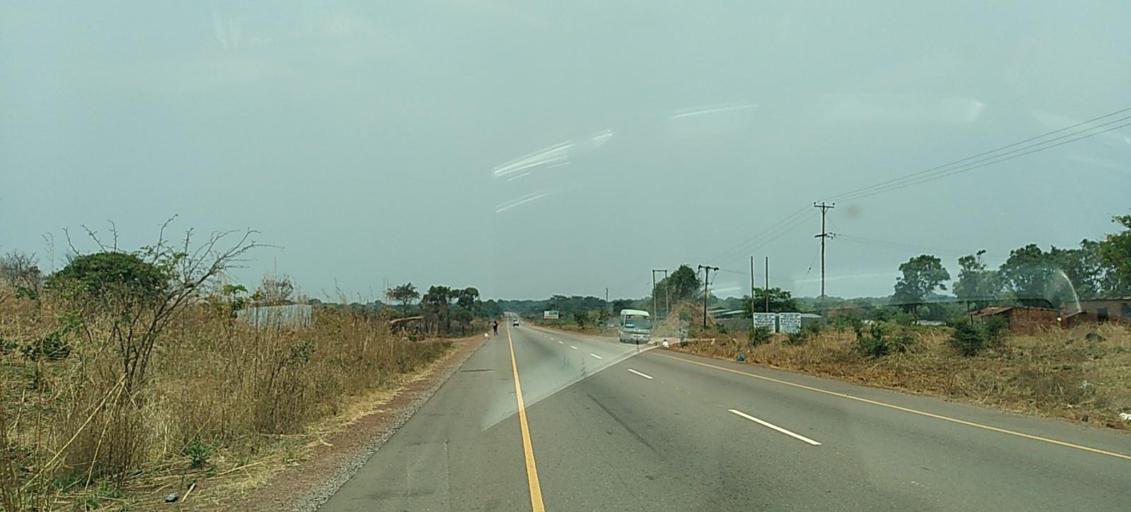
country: ZM
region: Copperbelt
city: Chingola
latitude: -12.5550
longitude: 27.7161
